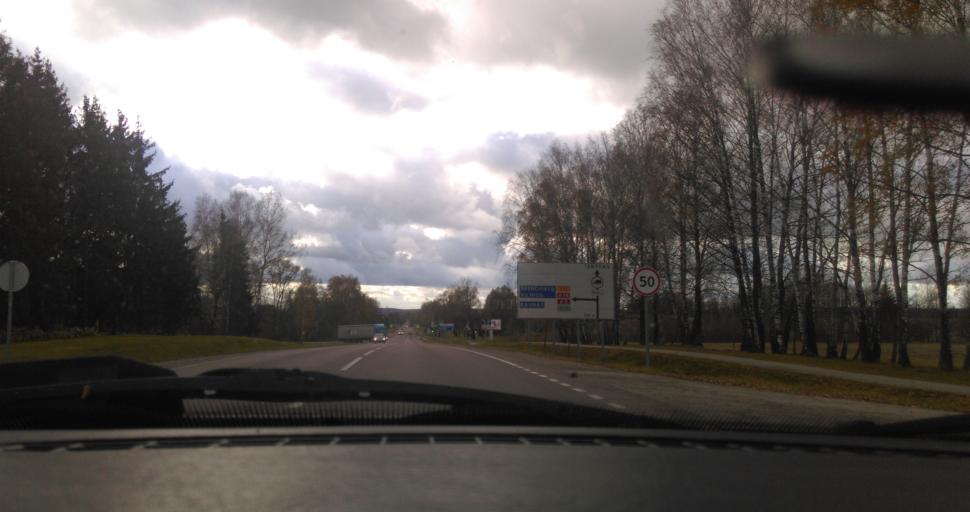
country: LT
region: Utenos apskritis
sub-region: Utena
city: Utena
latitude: 55.5084
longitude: 25.6323
